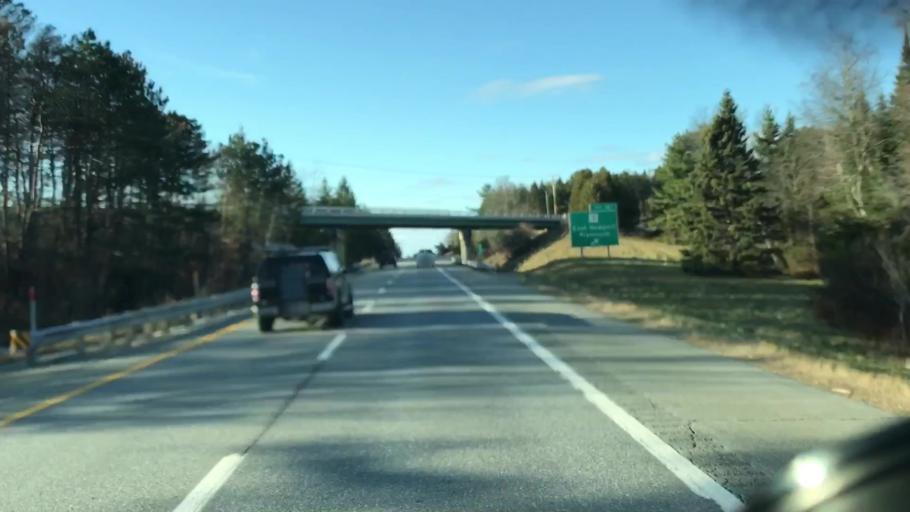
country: US
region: Maine
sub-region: Penobscot County
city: Plymouth
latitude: 44.8020
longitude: -69.2196
